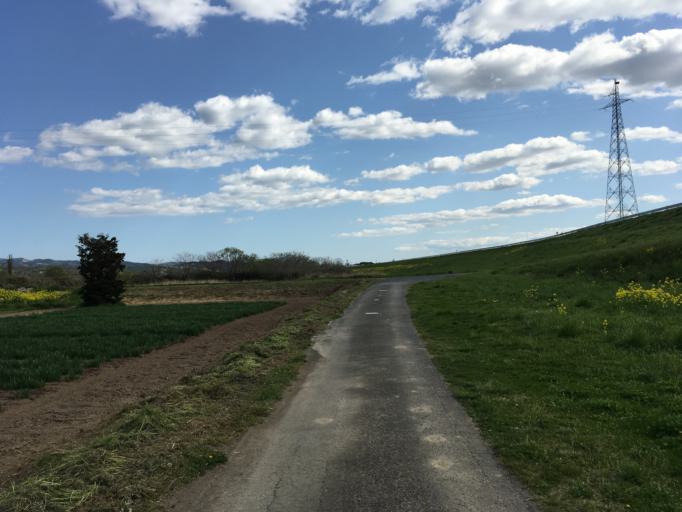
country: JP
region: Miyagi
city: Wakuya
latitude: 38.7162
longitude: 141.2650
